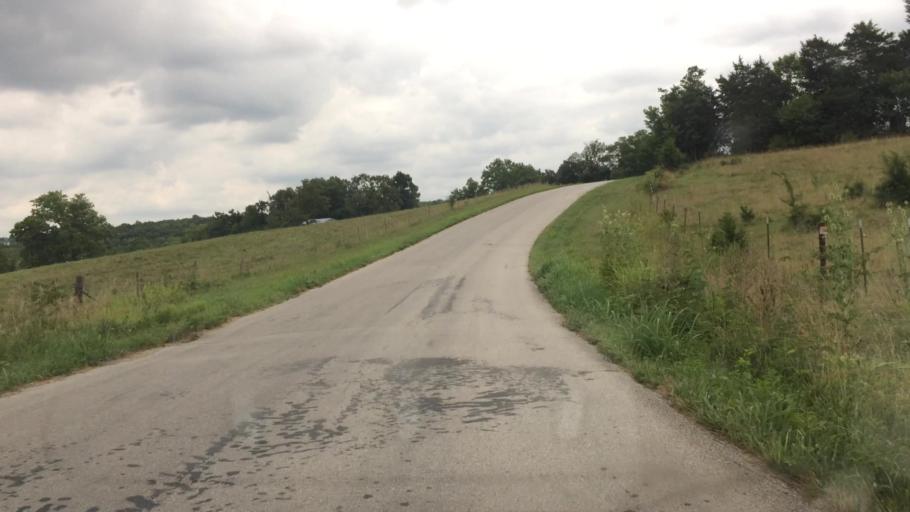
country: US
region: Missouri
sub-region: Greene County
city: Strafford
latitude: 37.3204
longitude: -93.0608
